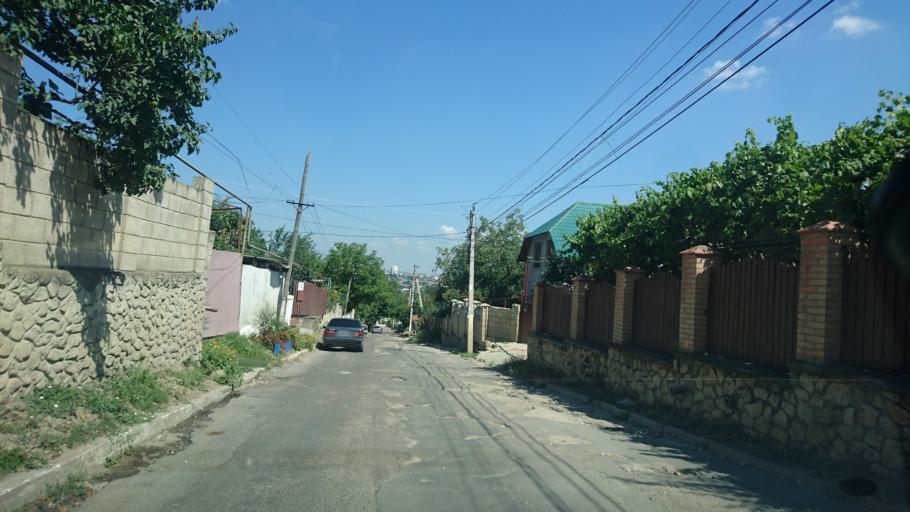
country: MD
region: Laloveni
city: Ialoveni
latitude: 47.0094
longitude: 28.7667
